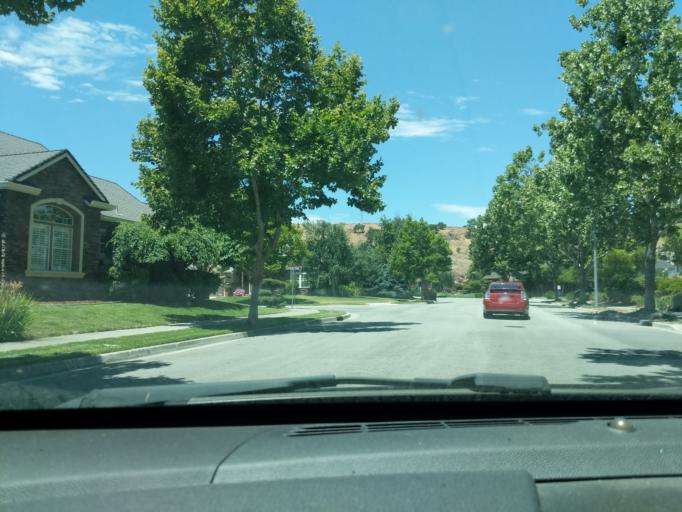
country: US
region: California
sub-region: Santa Clara County
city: Morgan Hill
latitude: 37.1367
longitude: -121.6707
